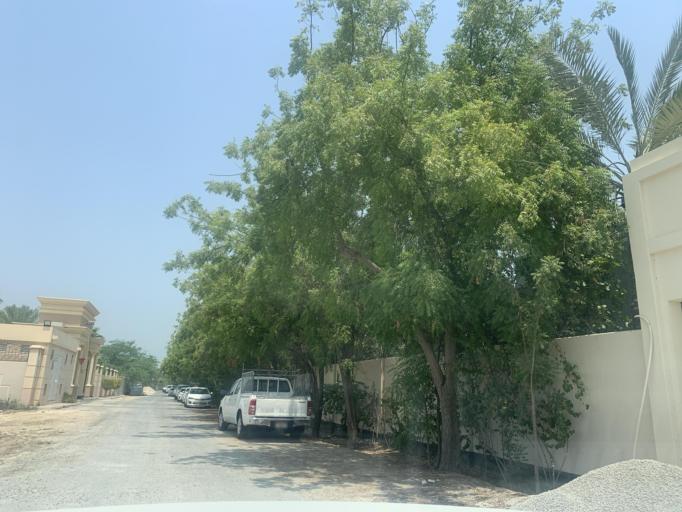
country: BH
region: Central Governorate
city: Madinat Hamad
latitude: 26.1481
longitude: 50.4648
